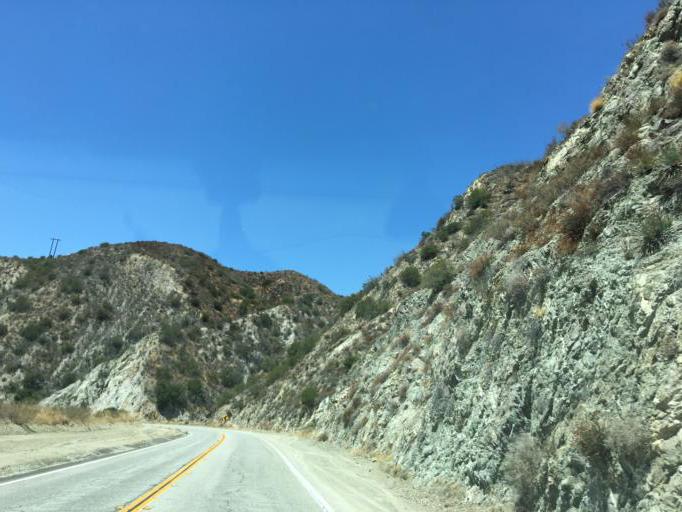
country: US
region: California
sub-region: Los Angeles County
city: La Crescenta-Montrose
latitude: 34.3051
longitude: -118.2621
